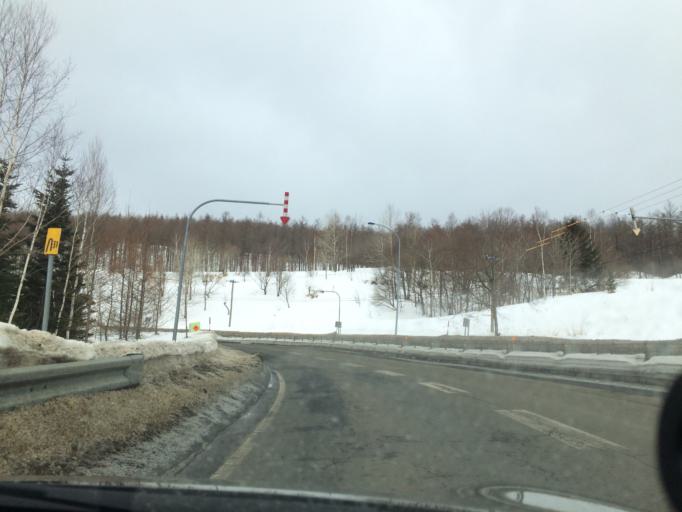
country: JP
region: Hokkaido
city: Shimo-furano
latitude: 42.8810
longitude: 142.2839
